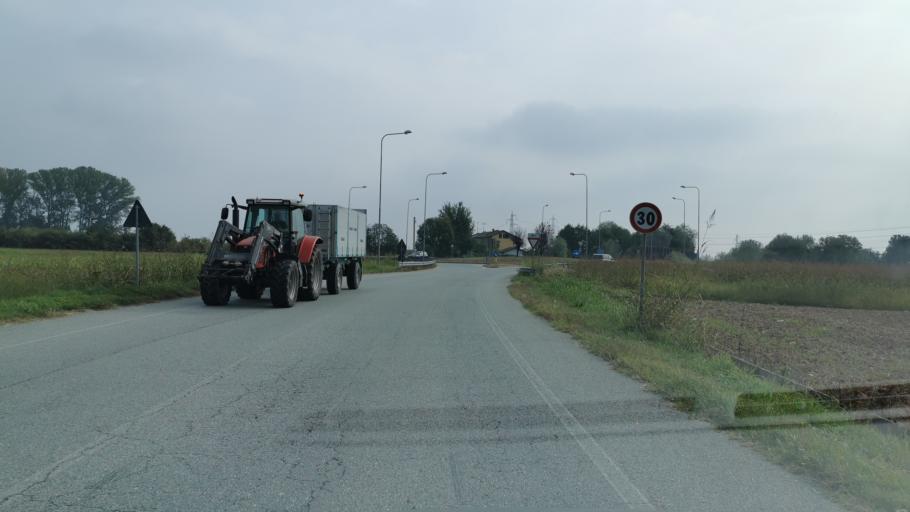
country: IT
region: Piedmont
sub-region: Provincia di Torino
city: Chivasso
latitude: 45.2292
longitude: 7.8947
